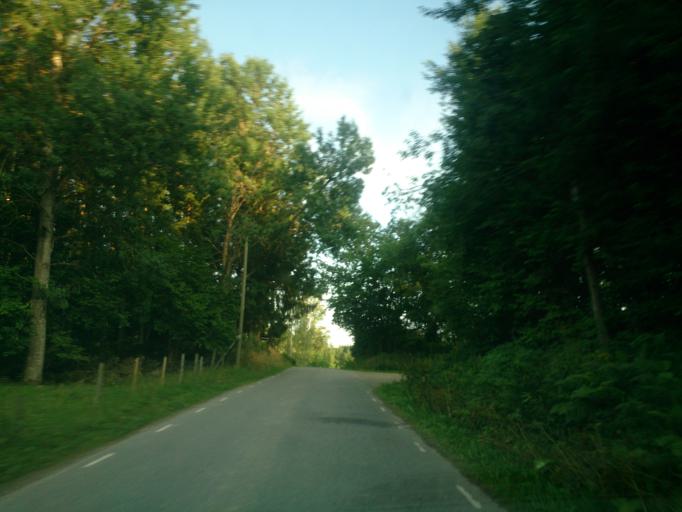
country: SE
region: OEstergoetland
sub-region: Atvidabergs Kommun
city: Atvidaberg
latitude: 58.2983
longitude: 16.0954
